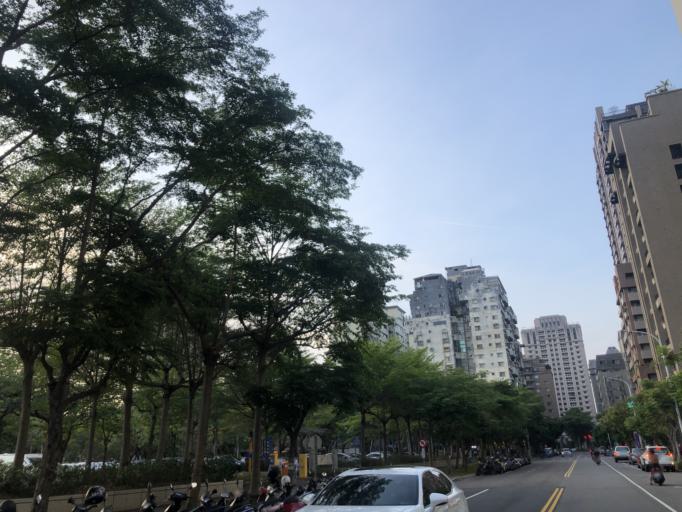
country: TW
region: Taiwan
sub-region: Taichung City
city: Taichung
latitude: 24.1297
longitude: 120.6451
